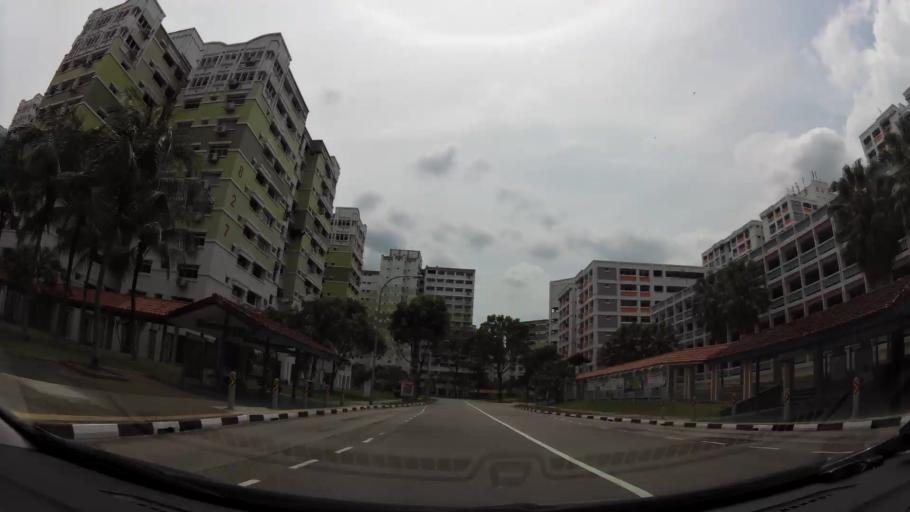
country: MY
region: Johor
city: Johor Bahru
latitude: 1.3459
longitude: 103.6928
